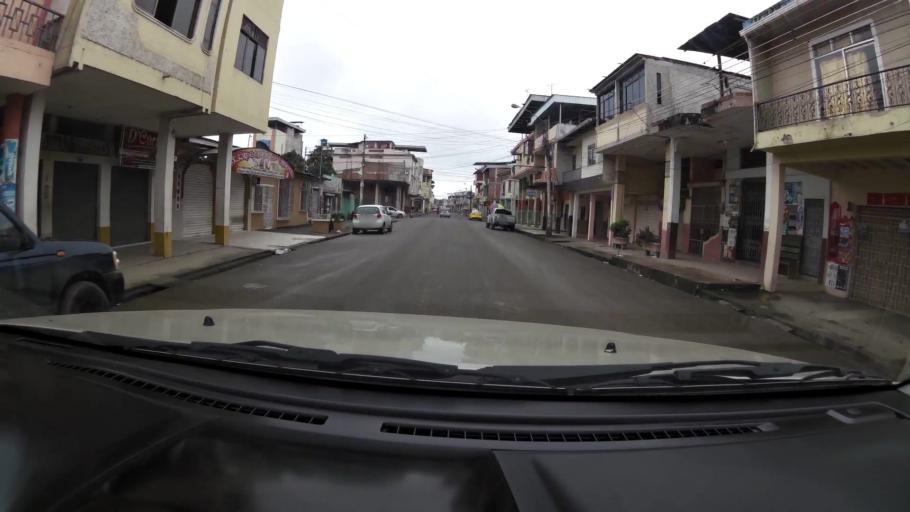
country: EC
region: El Oro
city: Pasaje
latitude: -3.3251
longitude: -79.8064
